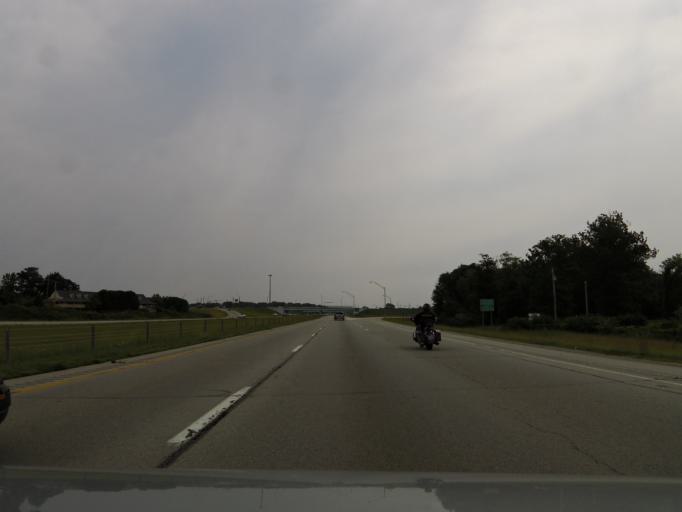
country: US
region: Ohio
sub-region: Montgomery County
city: Centerville
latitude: 39.6304
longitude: -84.2079
